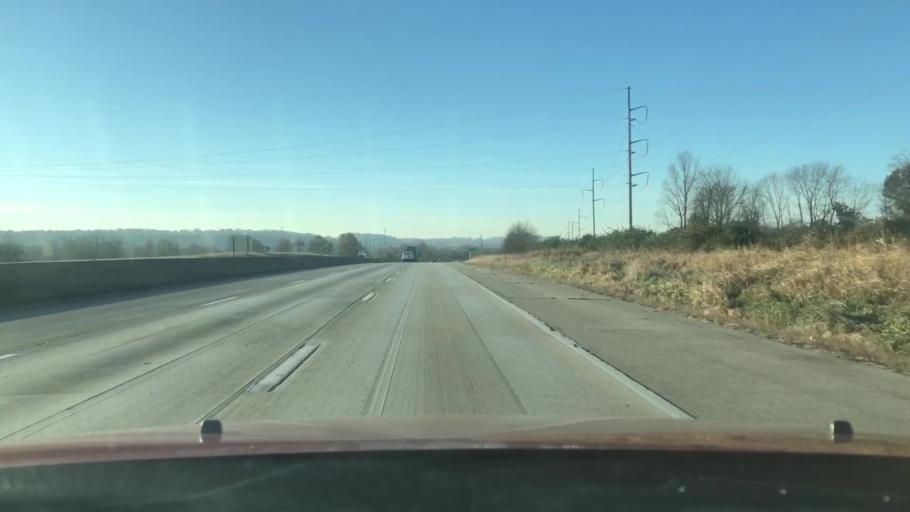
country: US
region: Missouri
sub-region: Greene County
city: Springfield
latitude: 37.1410
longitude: -93.2248
